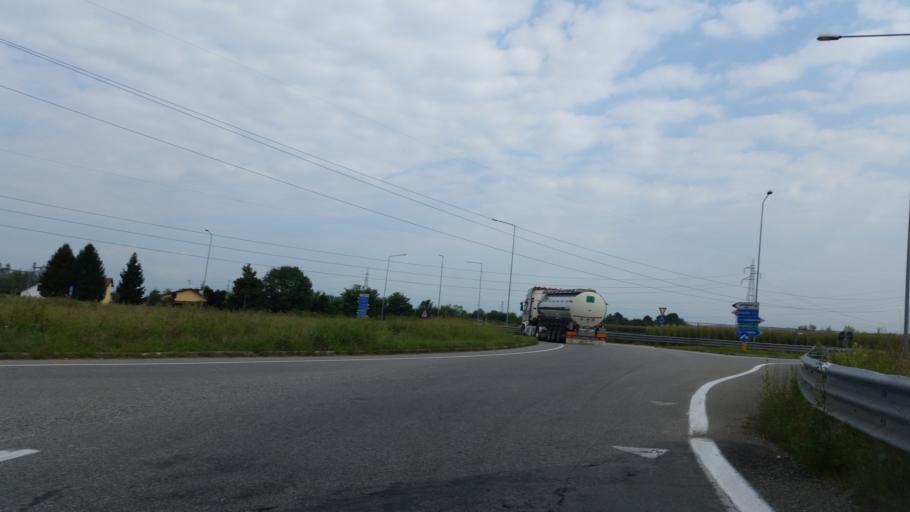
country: IT
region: Piedmont
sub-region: Provincia di Torino
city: Chivasso
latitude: 45.2263
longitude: 7.9151
